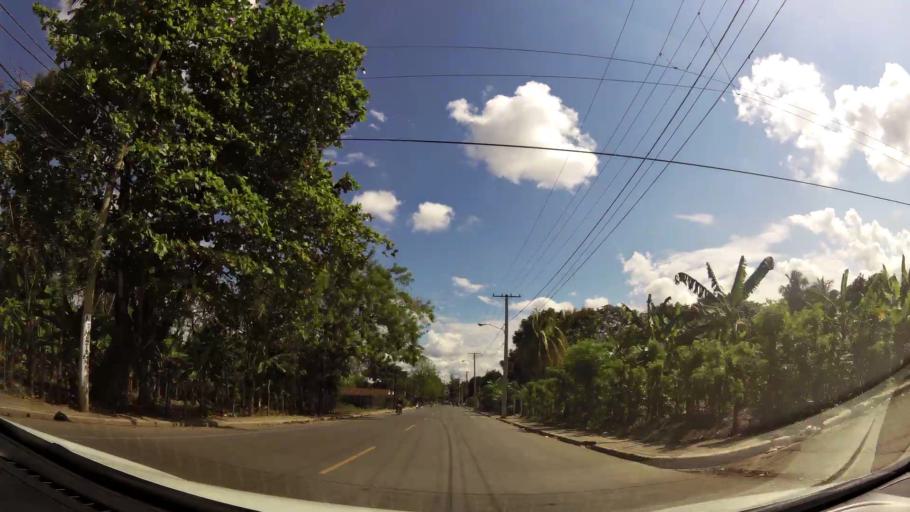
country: DO
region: La Vega
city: Concepcion de La Vega
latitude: 19.2445
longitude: -70.5377
